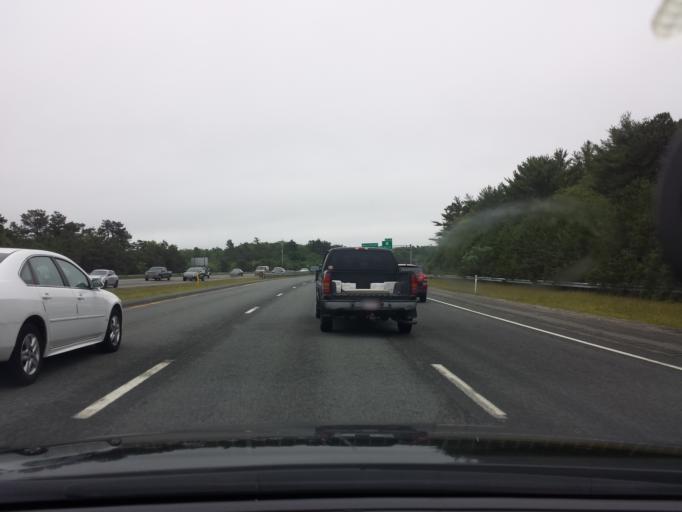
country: US
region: Massachusetts
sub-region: Barnstable County
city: Bourne
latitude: 41.7725
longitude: -70.5861
